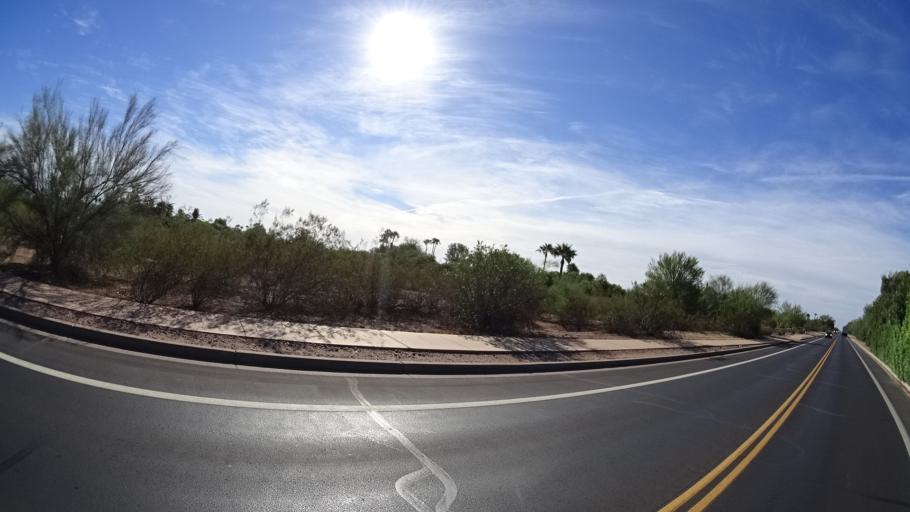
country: US
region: Arizona
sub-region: Maricopa County
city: Paradise Valley
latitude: 33.5225
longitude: -111.9432
